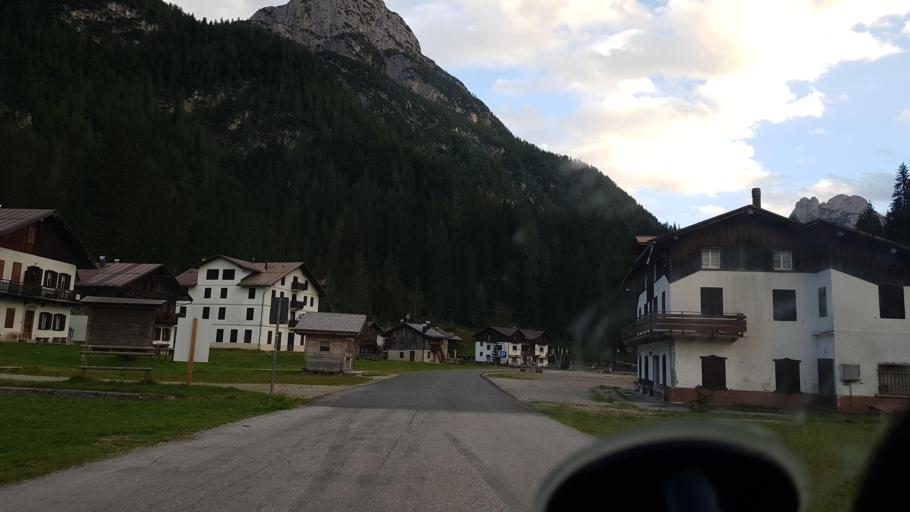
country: IT
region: Veneto
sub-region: Provincia di Belluno
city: San Pietro di Cadore
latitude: 46.6032
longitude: 12.6308
